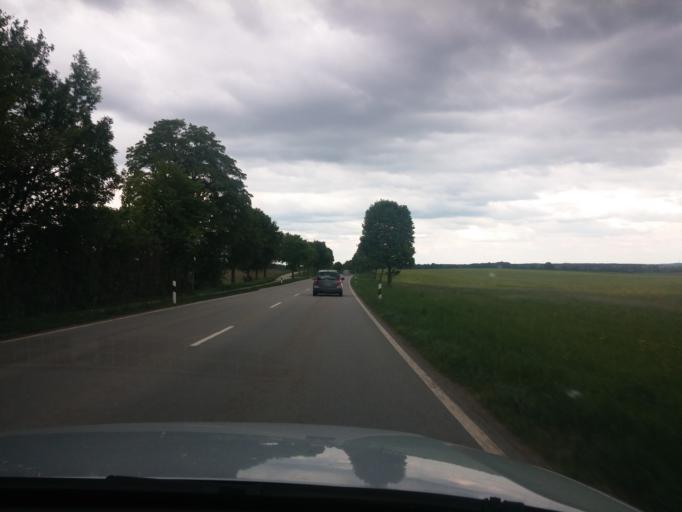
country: DE
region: Bavaria
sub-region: Upper Bavaria
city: Holzkirchen
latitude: 47.8507
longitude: 11.6829
